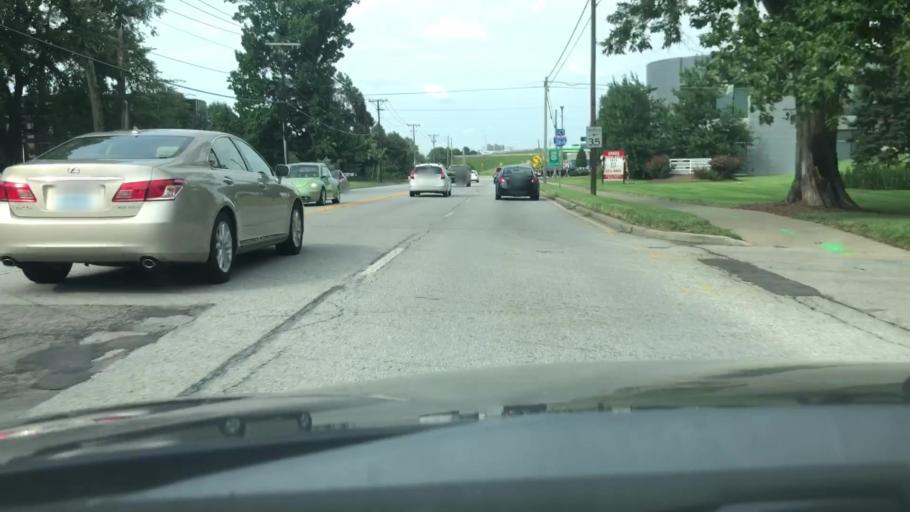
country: US
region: Kentucky
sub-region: Jefferson County
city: Lyndon
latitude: 38.2531
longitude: -85.6143
